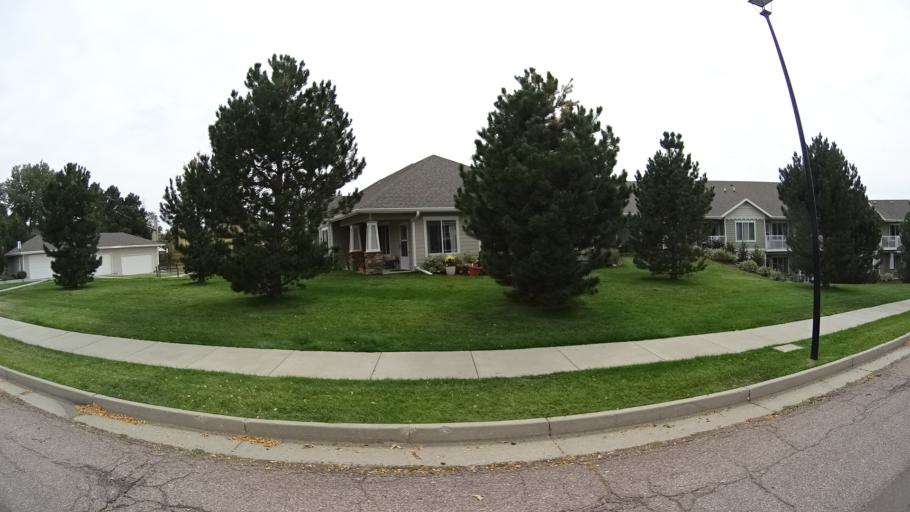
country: US
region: Colorado
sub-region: El Paso County
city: Cimarron Hills
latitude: 38.9055
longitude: -104.7369
